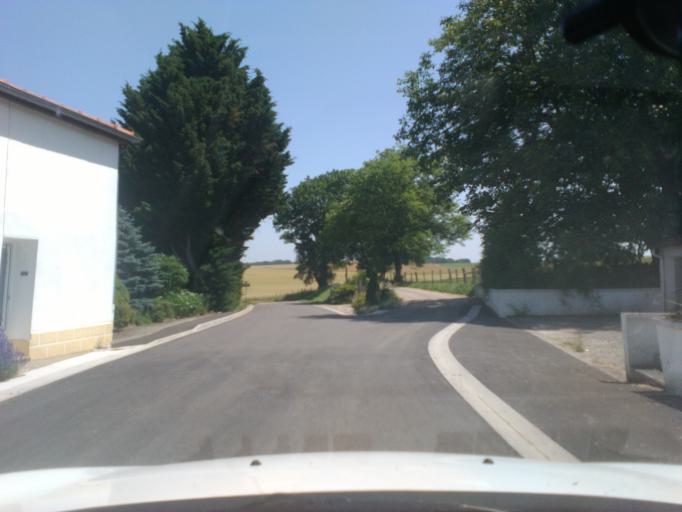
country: FR
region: Lorraine
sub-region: Departement de la Meuse
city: Gondrecourt-le-Chateau
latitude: 48.4230
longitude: 5.5286
